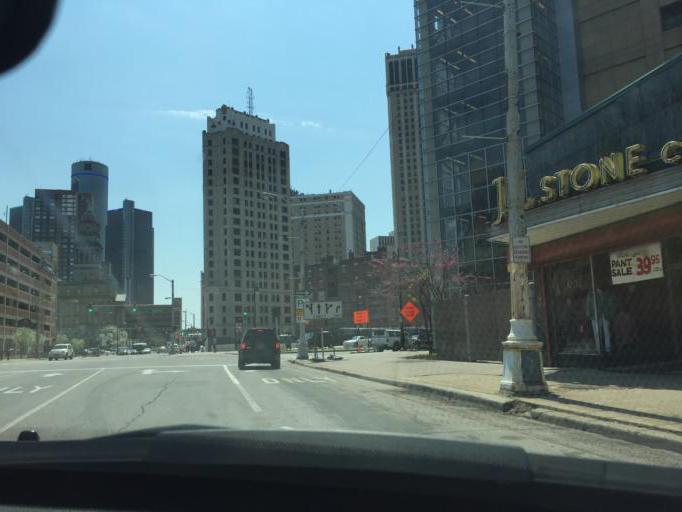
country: US
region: Michigan
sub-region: Wayne County
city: Detroit
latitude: 42.3343
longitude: -83.0451
